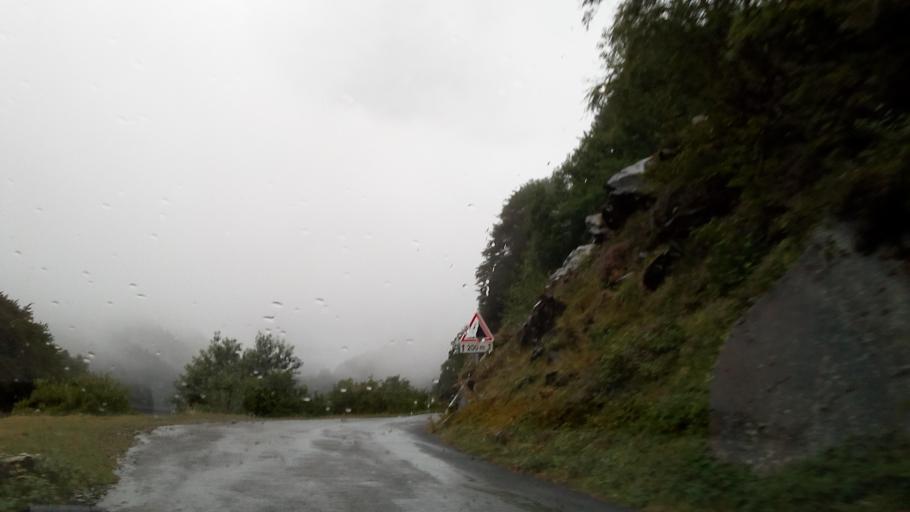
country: FR
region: Midi-Pyrenees
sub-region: Departement des Hautes-Pyrenees
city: Cauterets
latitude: 42.9194
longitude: -0.2533
